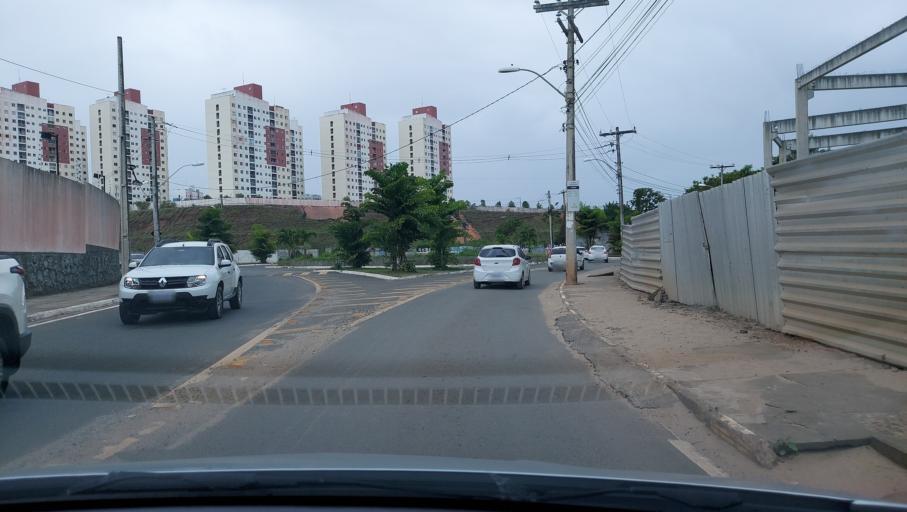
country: BR
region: Bahia
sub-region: Lauro De Freitas
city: Lauro de Freitas
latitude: -12.9385
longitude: -38.3798
